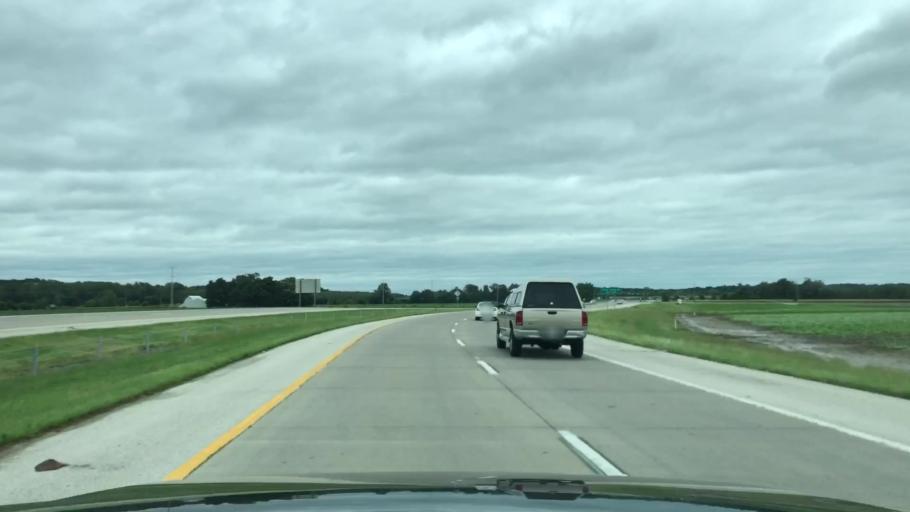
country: US
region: Missouri
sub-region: Saint Charles County
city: Saint Charles
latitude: 38.7214
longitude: -90.4982
